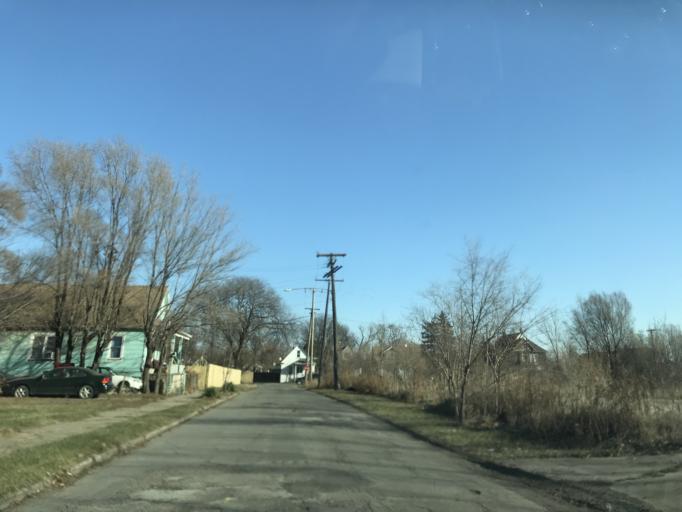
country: US
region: Michigan
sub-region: Wayne County
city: Dearborn
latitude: 42.3359
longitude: -83.1203
